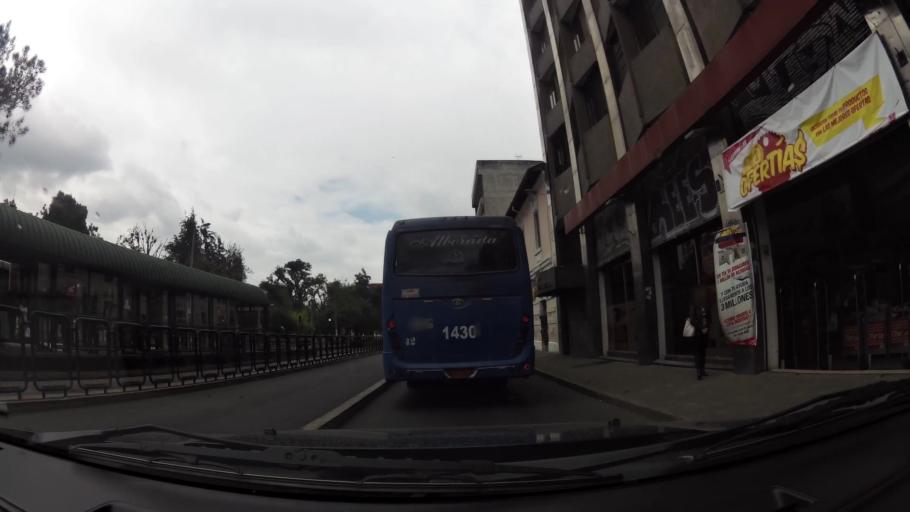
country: EC
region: Pichincha
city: Quito
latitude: -0.2158
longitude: -78.5027
